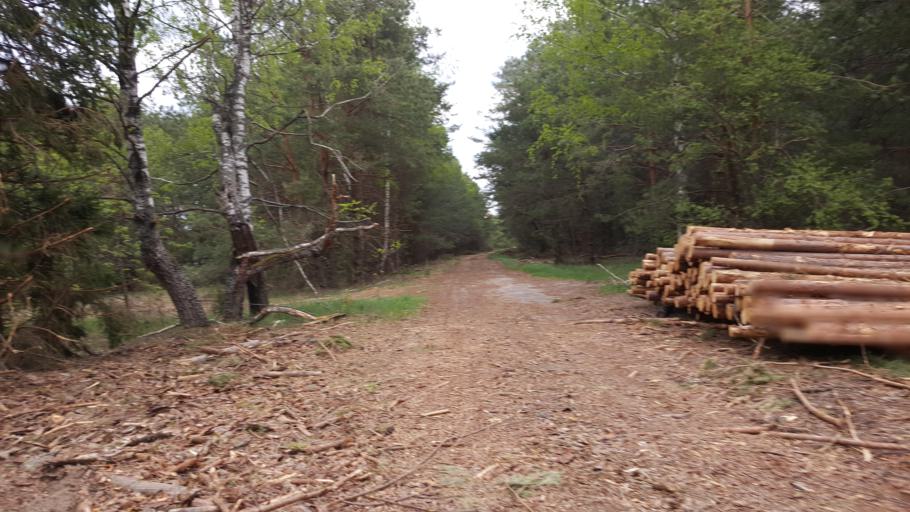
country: BY
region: Brest
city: Zhabinka
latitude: 52.3915
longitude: 24.0458
